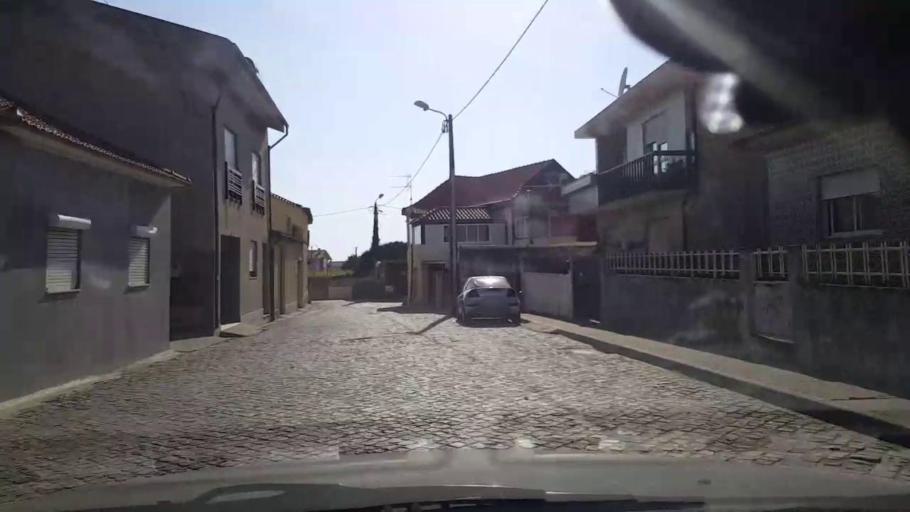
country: PT
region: Porto
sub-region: Vila do Conde
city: Vila do Conde
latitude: 41.3446
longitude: -8.7332
